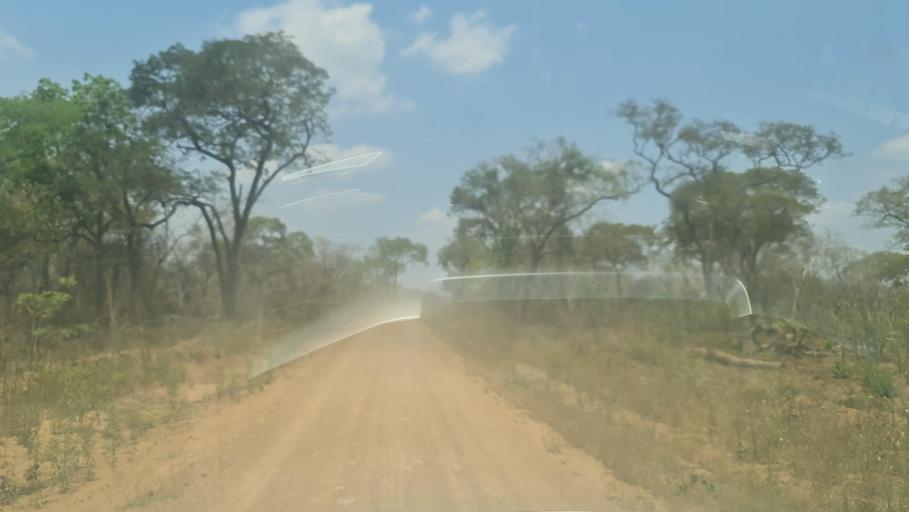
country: MW
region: Southern Region
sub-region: Nsanje District
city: Nsanje
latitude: -17.5592
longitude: 35.8987
